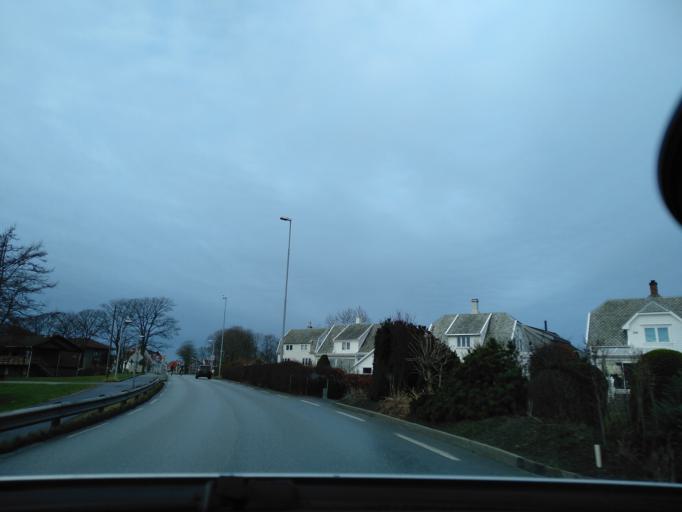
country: NO
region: Rogaland
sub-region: Randaberg
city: Randaberg
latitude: 58.9986
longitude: 5.6243
